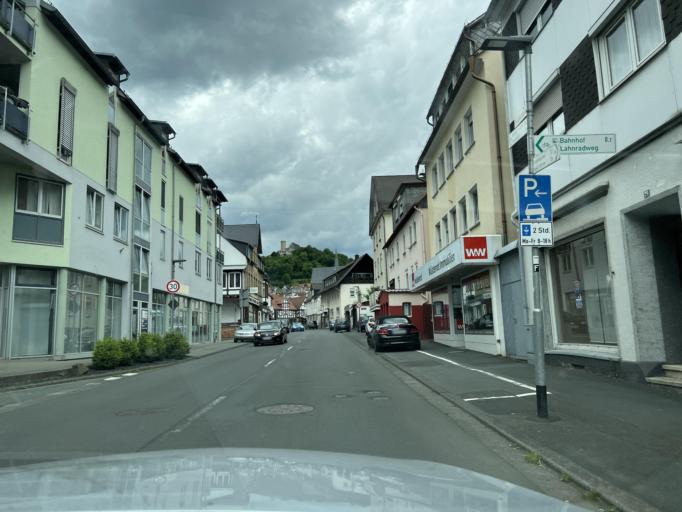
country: DE
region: Hesse
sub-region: Regierungsbezirk Giessen
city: Biedenkopf
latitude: 50.9094
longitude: 8.5316
